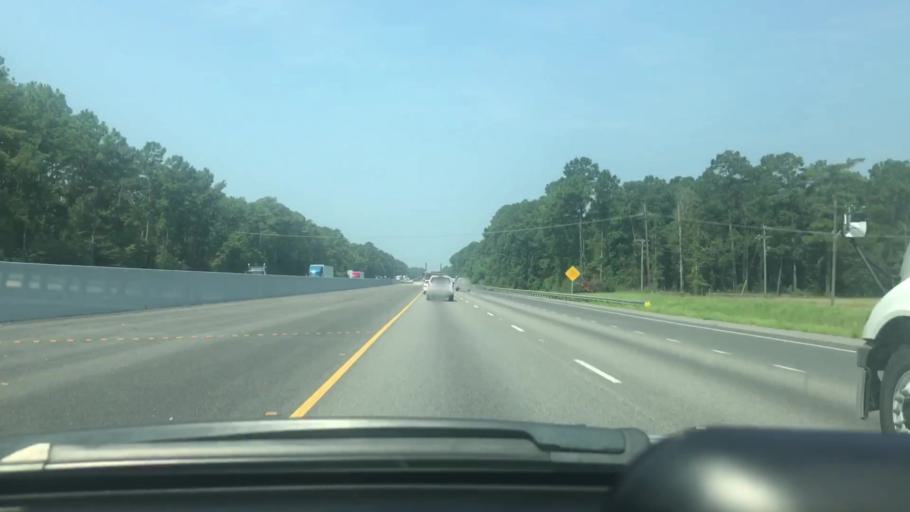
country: US
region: Louisiana
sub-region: Livingston Parish
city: Albany
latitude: 30.4747
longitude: -90.6497
